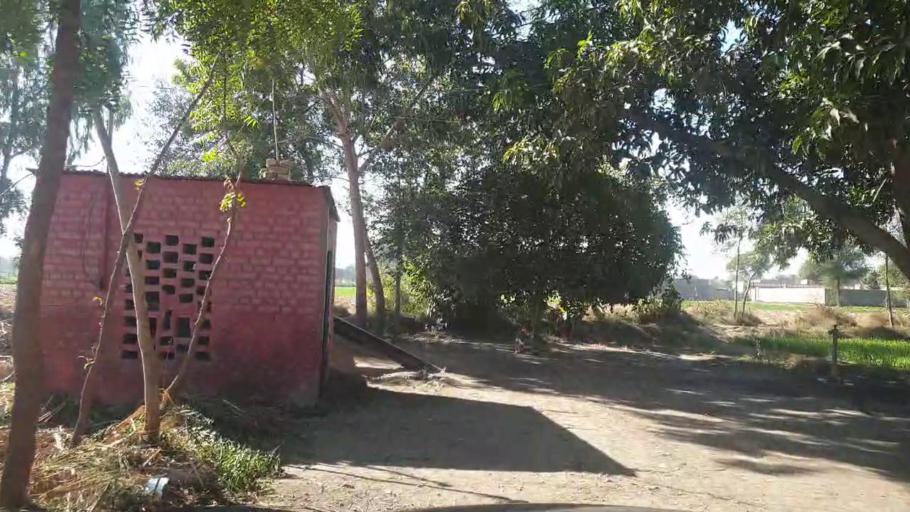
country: PK
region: Sindh
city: Adilpur
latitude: 27.9662
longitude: 69.3324
